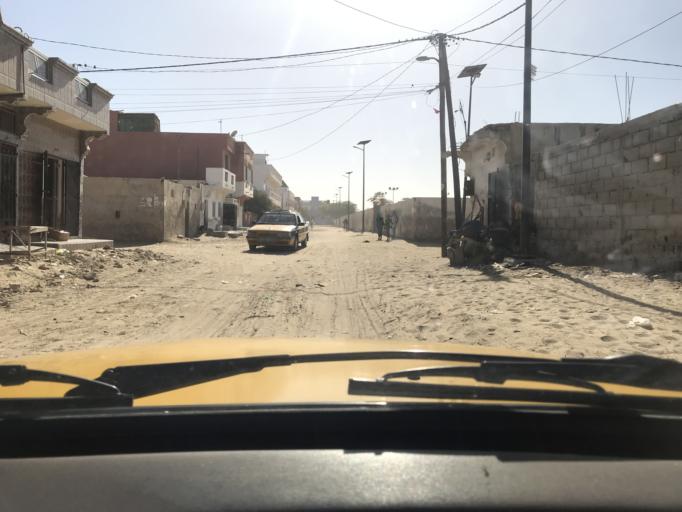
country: SN
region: Saint-Louis
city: Saint-Louis
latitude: 16.0074
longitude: -16.4866
